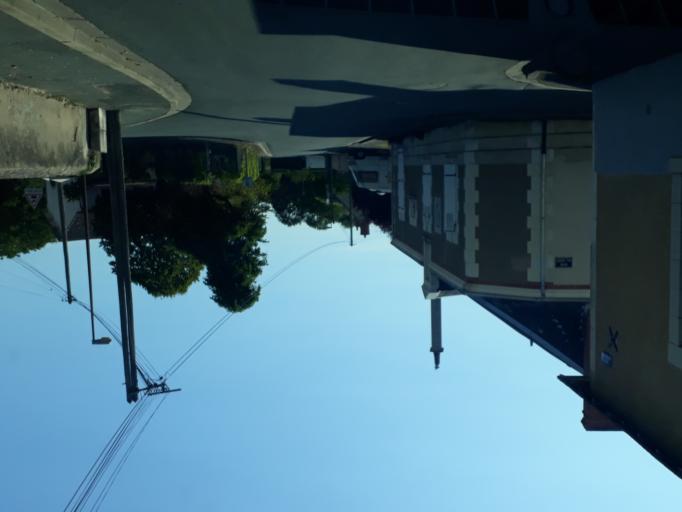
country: FR
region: Centre
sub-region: Departement de l'Indre
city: Chabris
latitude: 47.2572
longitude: 1.6491
